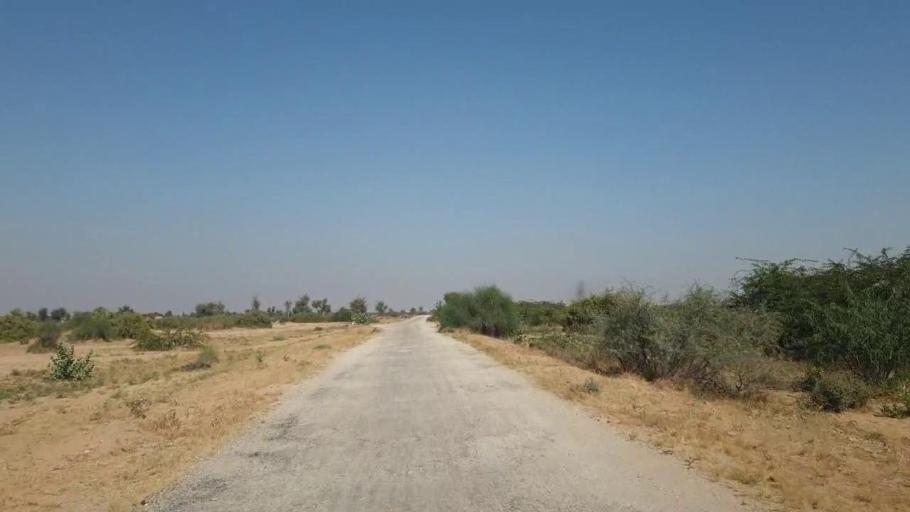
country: PK
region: Sindh
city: Jamshoro
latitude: 25.3843
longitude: 67.8459
